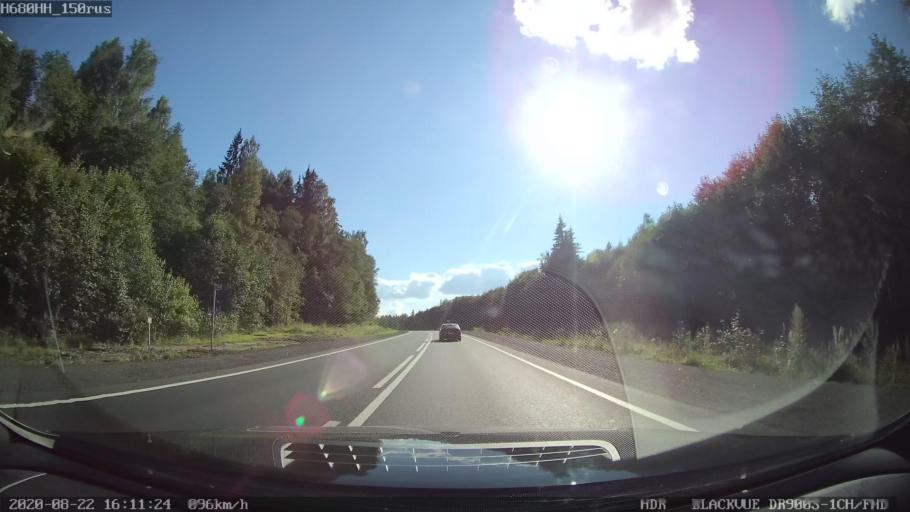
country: RU
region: Tverskaya
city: Rameshki
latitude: 57.5017
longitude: 36.2620
